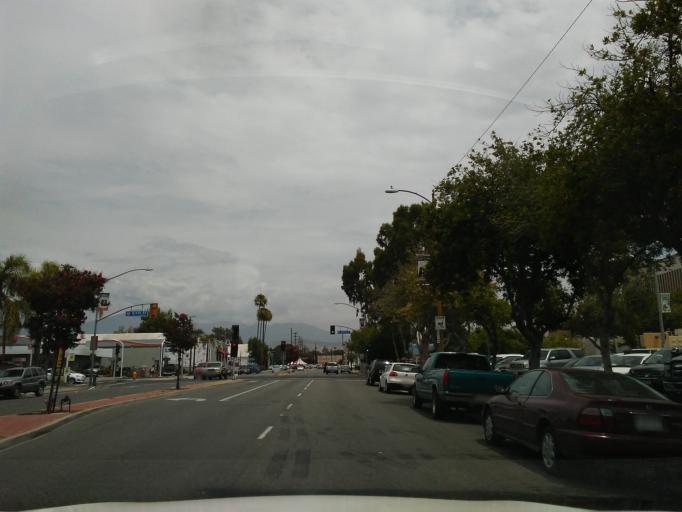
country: US
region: California
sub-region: San Bernardino County
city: Redlands
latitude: 34.0573
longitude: -117.1811
